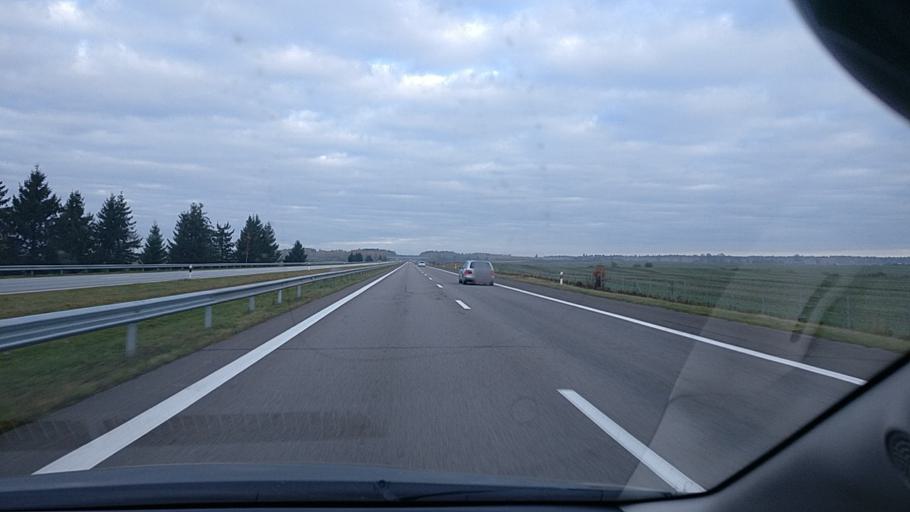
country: LT
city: Sirvintos
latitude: 54.9369
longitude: 24.9778
